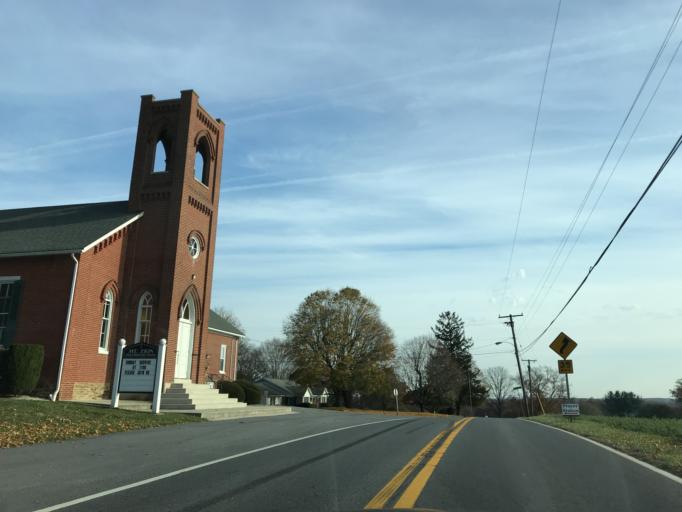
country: US
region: Maryland
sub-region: Carroll County
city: Hampstead
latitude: 39.5748
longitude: -76.7806
